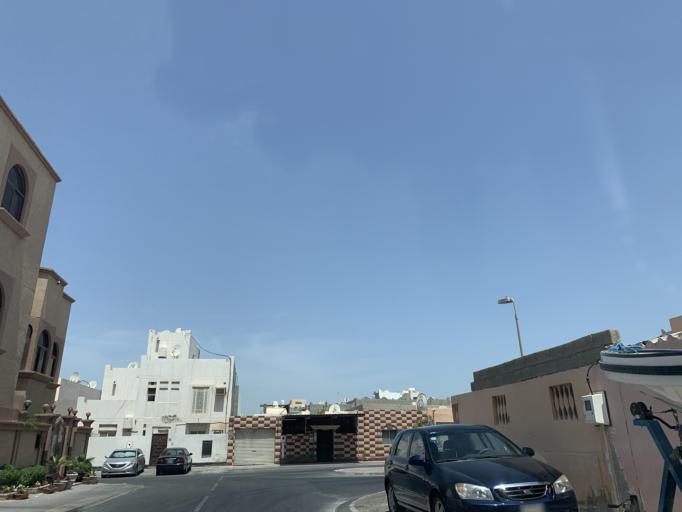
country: BH
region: Northern
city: Ar Rifa'
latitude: 26.1388
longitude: 50.5675
